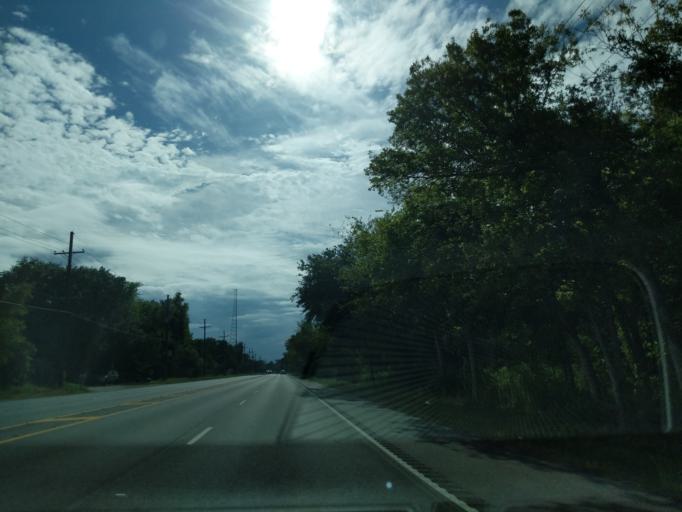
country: US
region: Louisiana
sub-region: Saint Bernard Parish
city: Meraux
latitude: 30.0501
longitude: -89.8838
